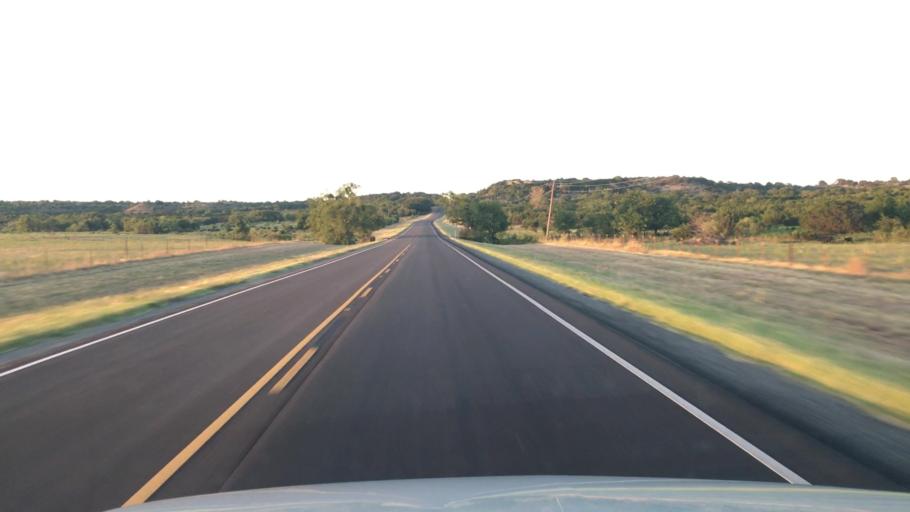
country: US
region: Texas
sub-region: Hamilton County
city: Hico
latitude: 32.0893
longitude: -97.9727
